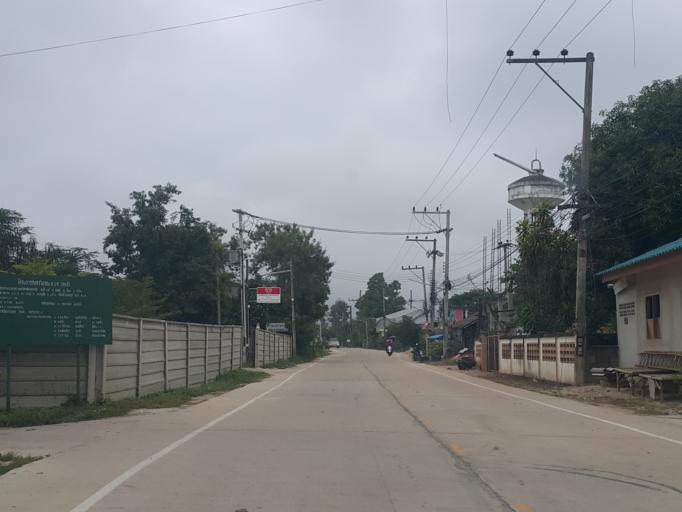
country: TH
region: Lampang
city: Lampang
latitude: 18.3196
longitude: 99.4909
